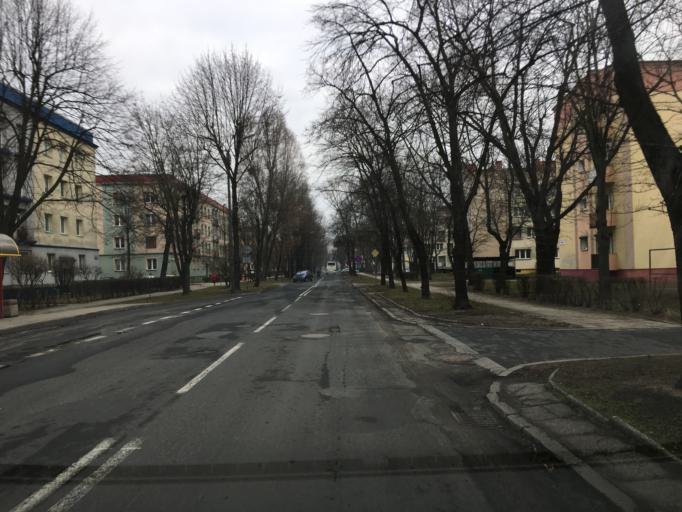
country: PL
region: Opole Voivodeship
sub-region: Powiat kedzierzynsko-kozielski
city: Kedzierzyn-Kozle
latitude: 50.3420
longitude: 18.2171
